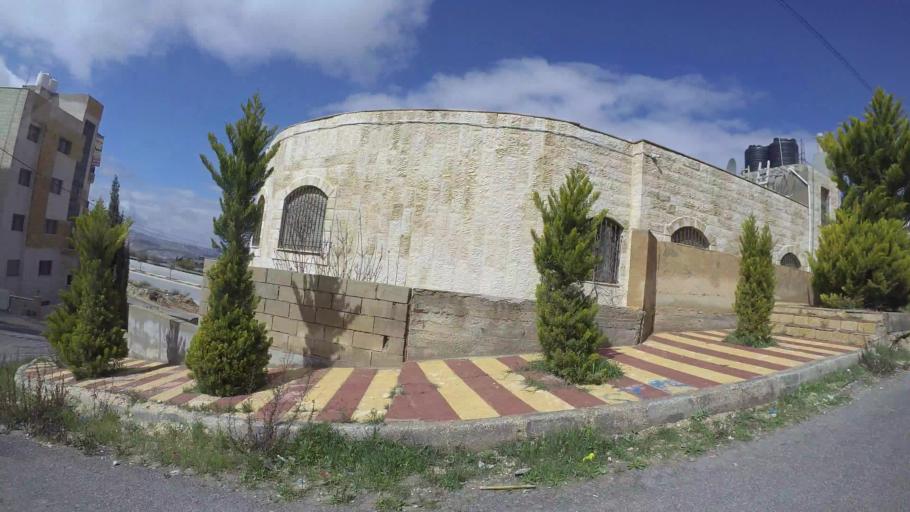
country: JO
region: Amman
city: Al Jubayhah
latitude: 32.0662
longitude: 35.8720
